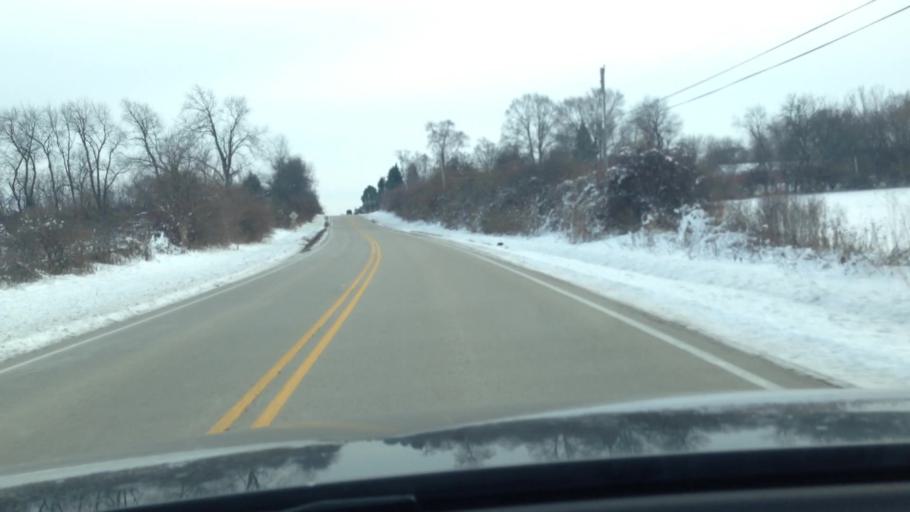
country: US
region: Illinois
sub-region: McHenry County
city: Woodstock
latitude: 42.3864
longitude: -88.4433
